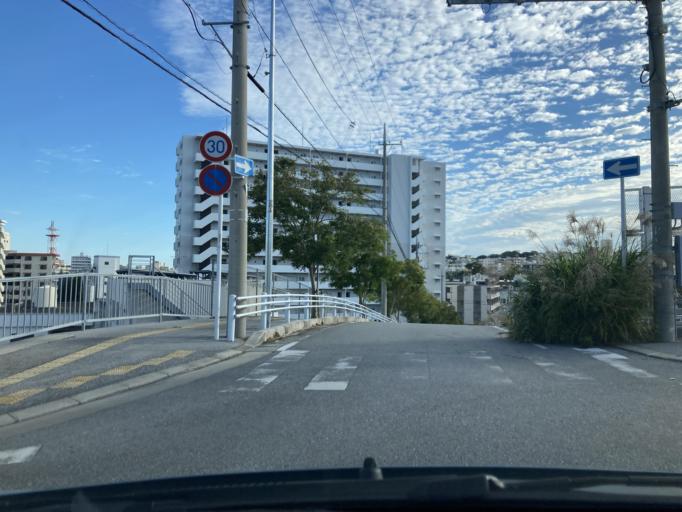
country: JP
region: Okinawa
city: Ginowan
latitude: 26.2637
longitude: 127.7304
